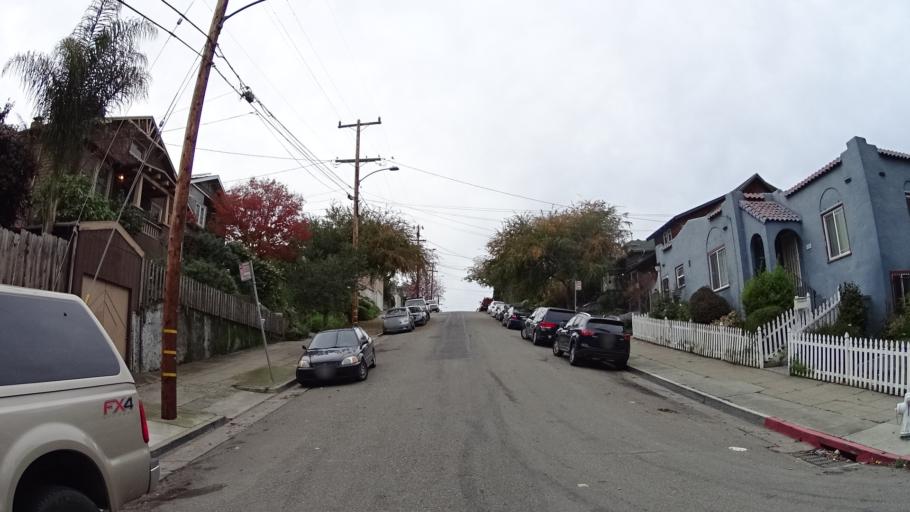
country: US
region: California
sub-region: Alameda County
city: Piedmont
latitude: 37.7980
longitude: -122.2333
